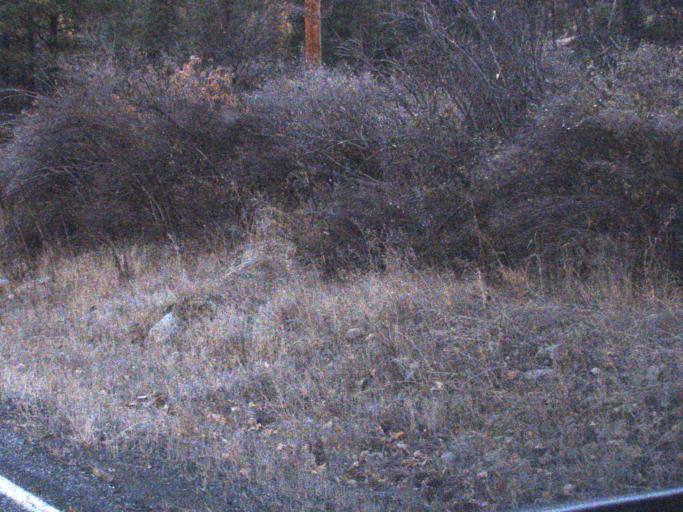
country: US
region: Washington
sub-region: Ferry County
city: Republic
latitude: 48.3946
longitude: -118.7406
